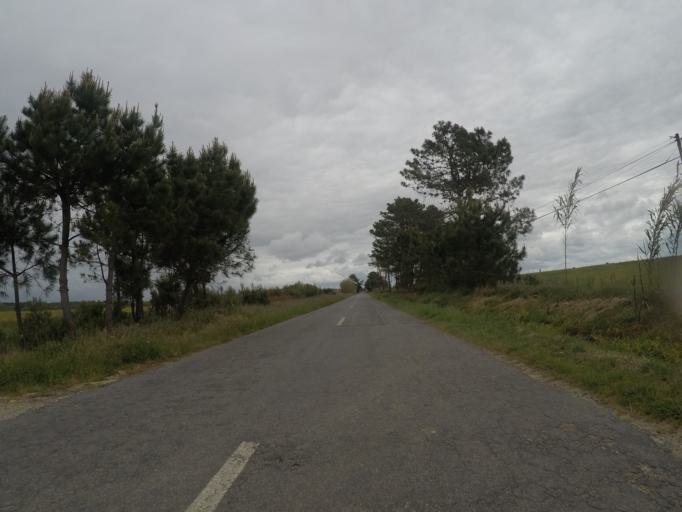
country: PT
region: Beja
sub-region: Odemira
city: Vila Nova de Milfontes
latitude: 37.6013
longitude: -8.8037
